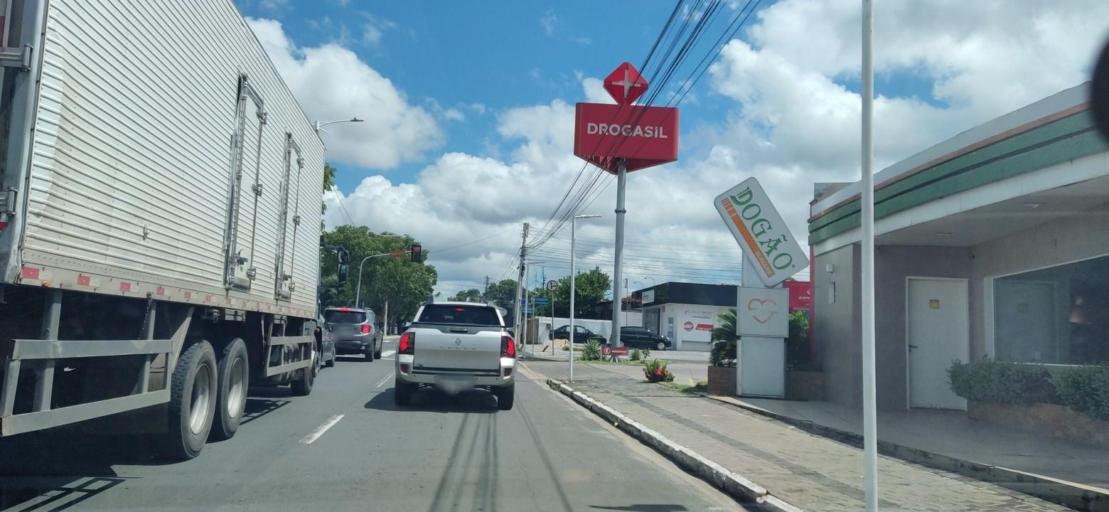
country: BR
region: Piaui
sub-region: Teresina
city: Teresina
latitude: -5.0637
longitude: -42.7940
